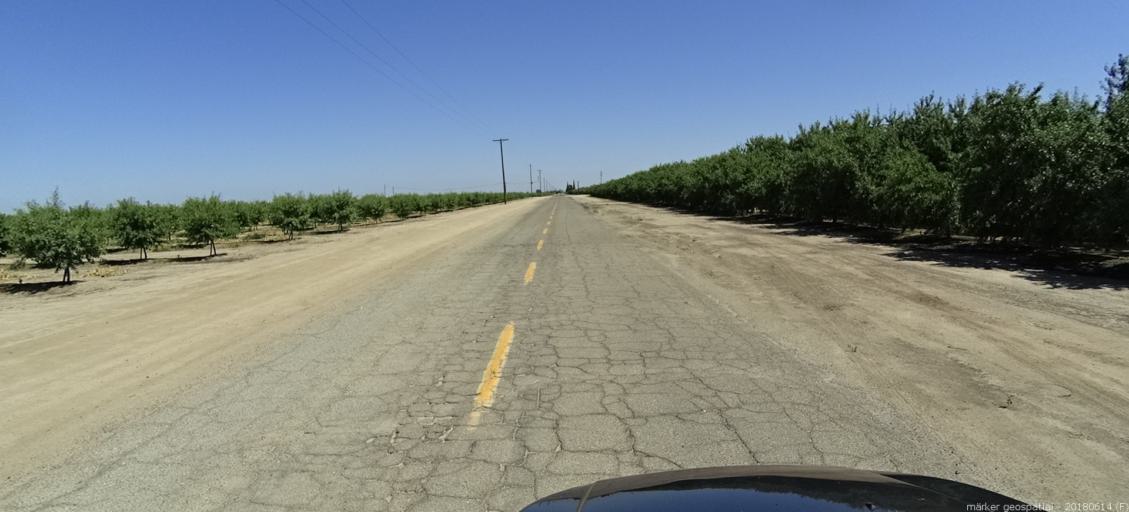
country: US
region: California
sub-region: Madera County
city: Fairmead
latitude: 36.9578
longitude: -120.1840
